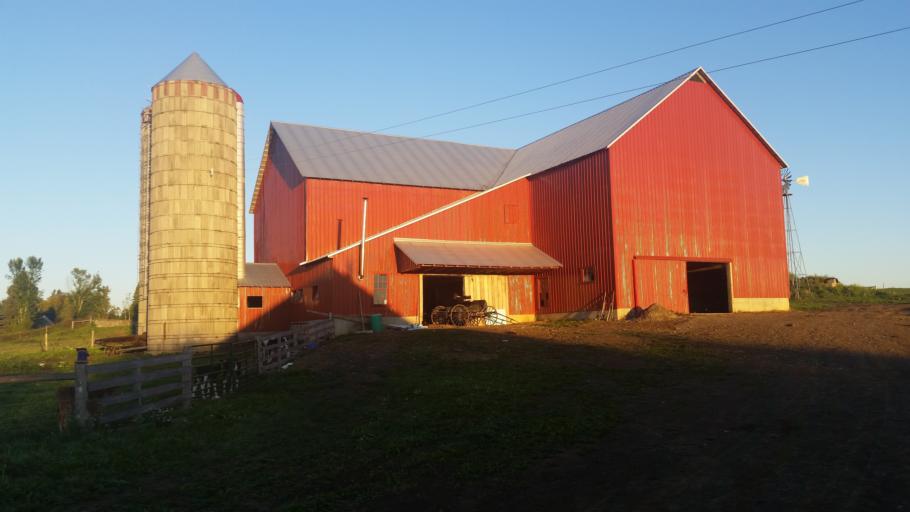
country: US
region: Maine
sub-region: Aroostook County
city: Easton
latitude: 46.6742
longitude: -67.8205
